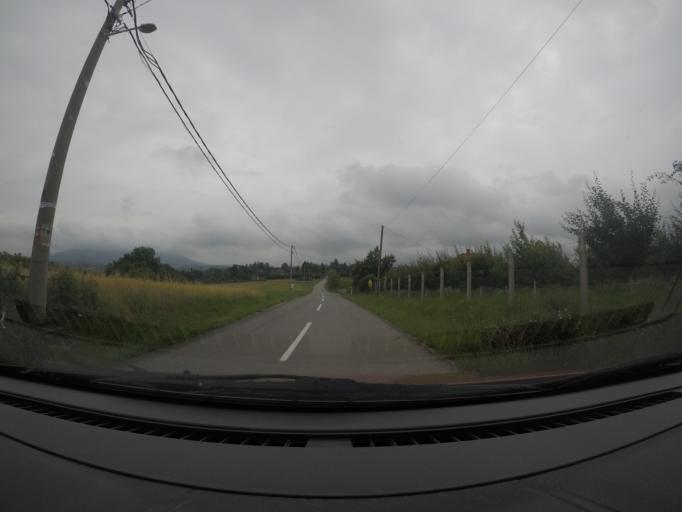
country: RS
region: Central Serbia
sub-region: Belgrade
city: Sopot
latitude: 44.5269
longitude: 20.5396
